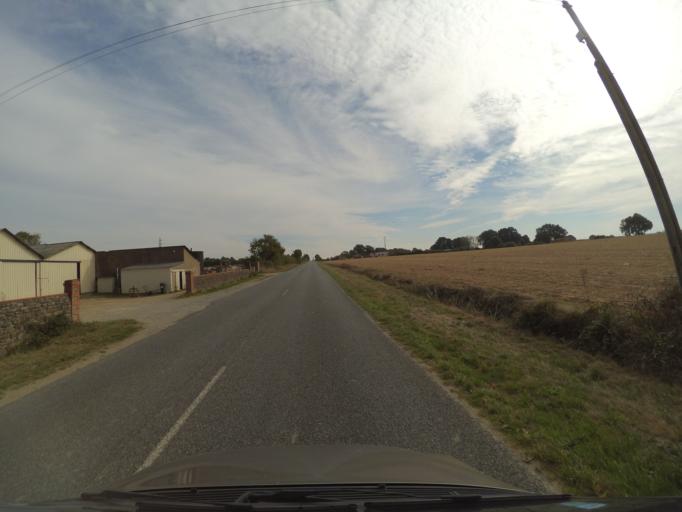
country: FR
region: Pays de la Loire
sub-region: Departement de Maine-et-Loire
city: Chemille-Melay
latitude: 47.2117
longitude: -0.7569
